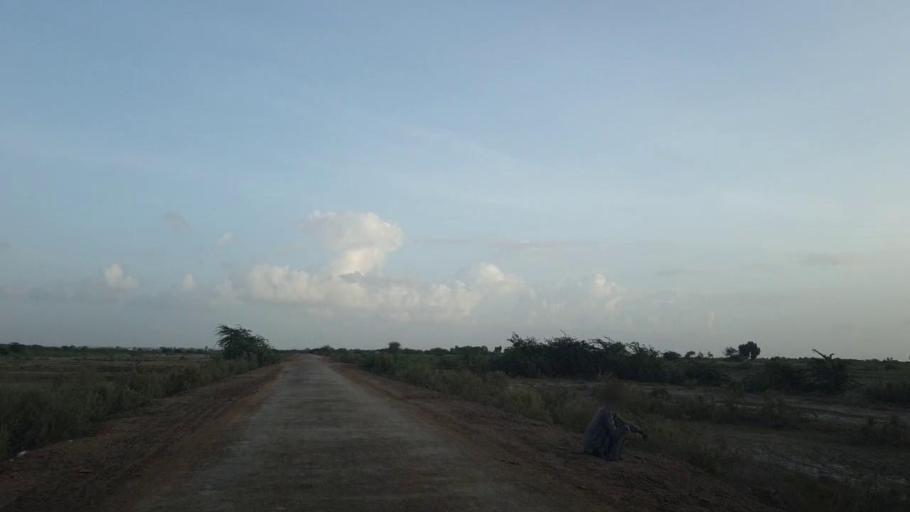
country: PK
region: Sindh
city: Kadhan
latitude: 24.5622
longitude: 69.1215
